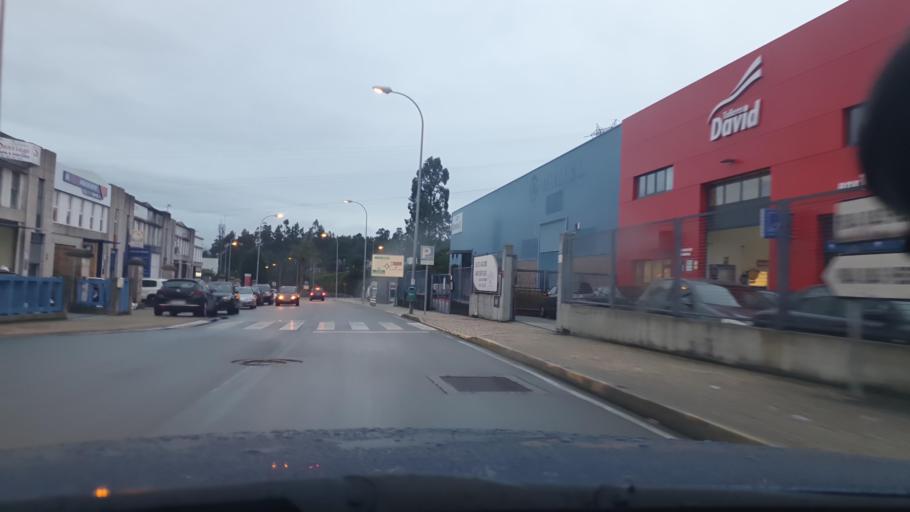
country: ES
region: Galicia
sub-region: Provincia da Coruna
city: Santiago de Compostela
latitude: 42.8512
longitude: -8.5821
